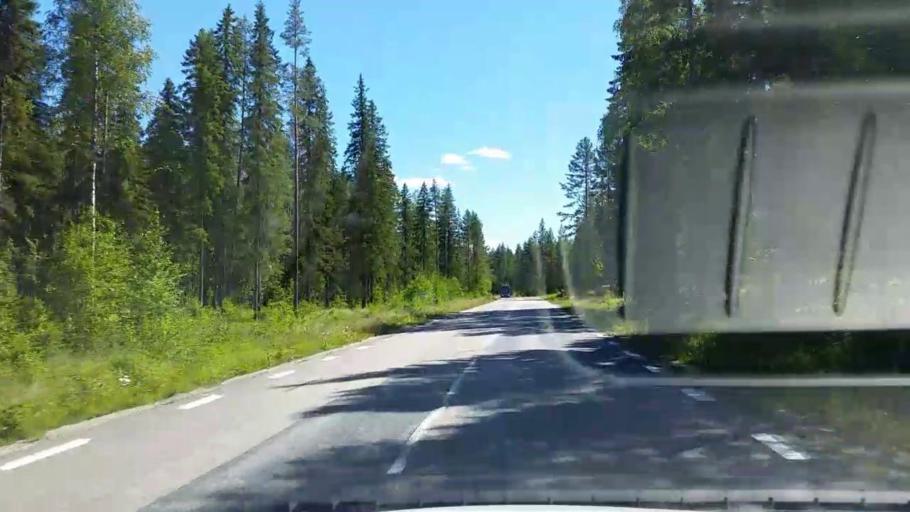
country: SE
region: Gaevleborg
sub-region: Ovanakers Kommun
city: Edsbyn
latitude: 61.3426
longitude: 15.8208
